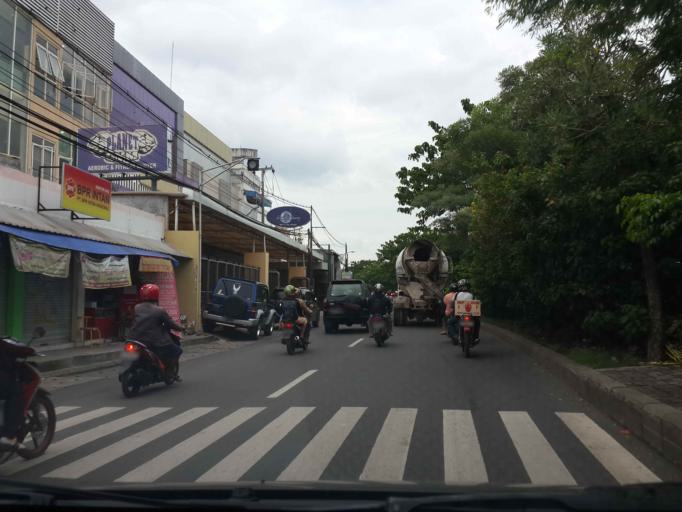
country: ID
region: East Java
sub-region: Kota Surabaya
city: Surabaya
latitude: -7.2699
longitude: 112.7184
